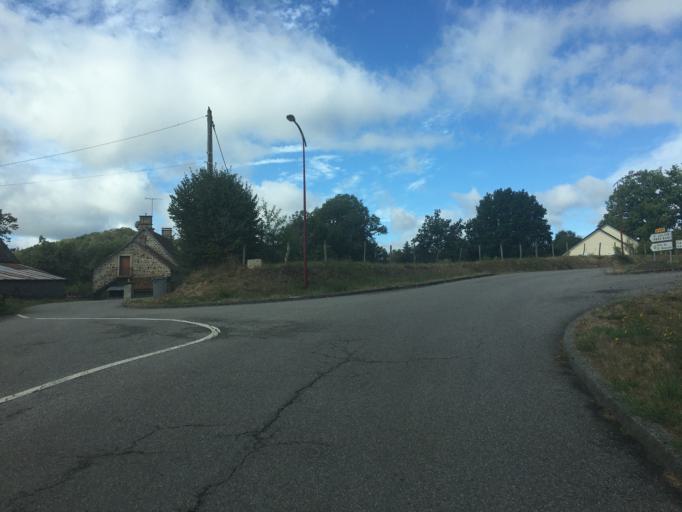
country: FR
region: Auvergne
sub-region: Departement du Cantal
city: Champagnac
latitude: 45.4138
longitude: 2.4294
